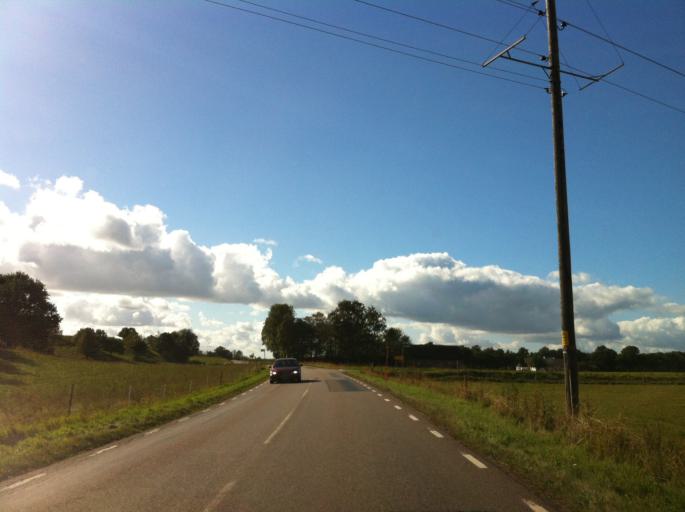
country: SE
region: Skane
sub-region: Sjobo Kommun
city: Sjoebo
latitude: 55.6377
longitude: 13.7572
